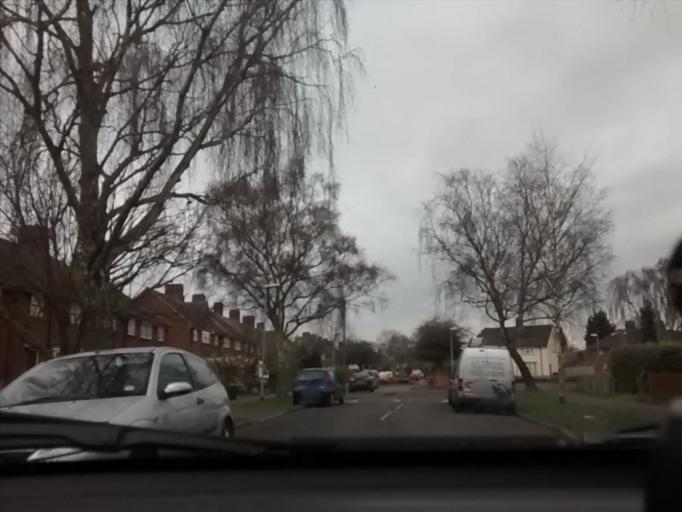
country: GB
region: England
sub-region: Cambridgeshire
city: Cambridge
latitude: 52.2156
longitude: 0.1610
